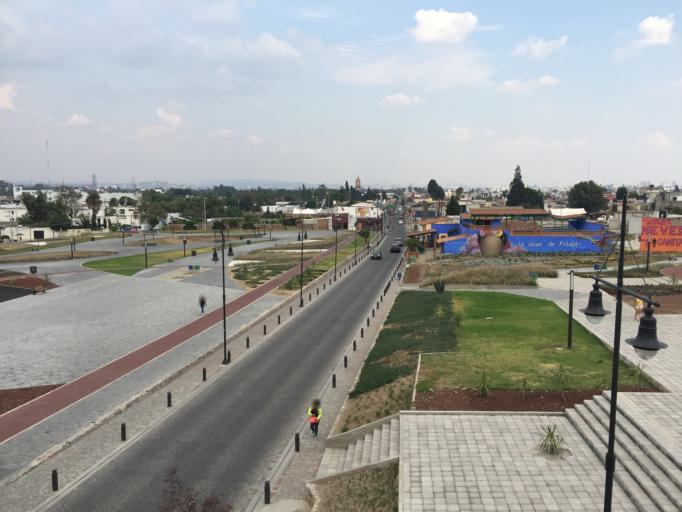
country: MX
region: Puebla
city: Cholula
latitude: 19.0585
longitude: -98.2996
